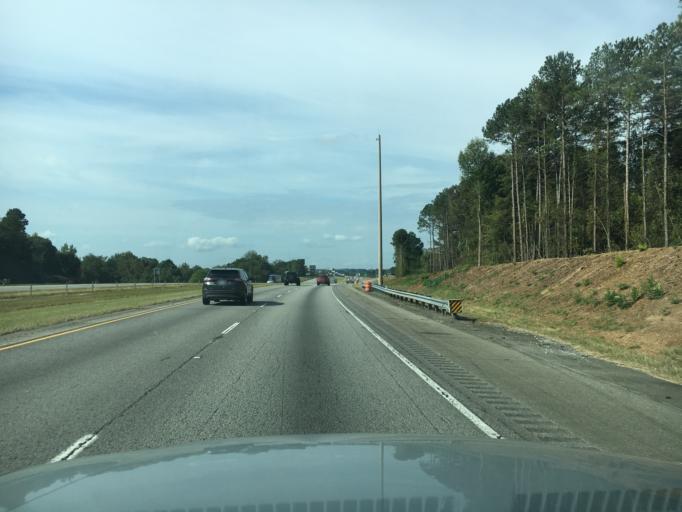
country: US
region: Georgia
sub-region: Franklin County
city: Lavonia
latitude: 34.4181
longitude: -83.1699
